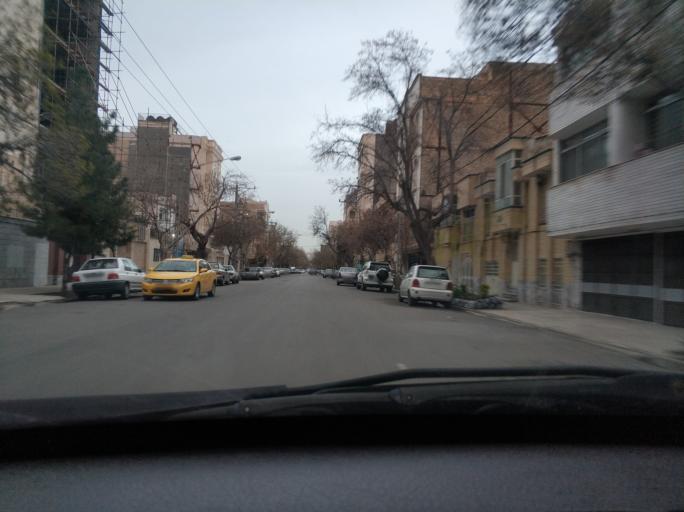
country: IR
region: Razavi Khorasan
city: Mashhad
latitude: 36.2743
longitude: 59.5964
